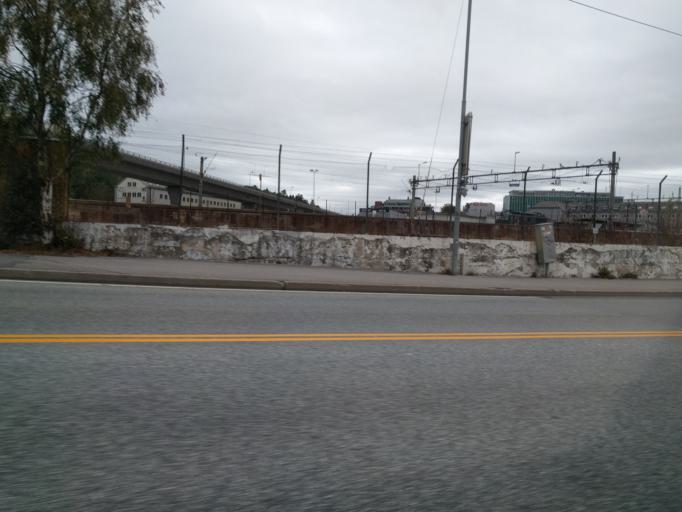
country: NO
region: Vest-Agder
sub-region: Kristiansand
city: Kristiansand
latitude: 58.1454
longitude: 7.9840
